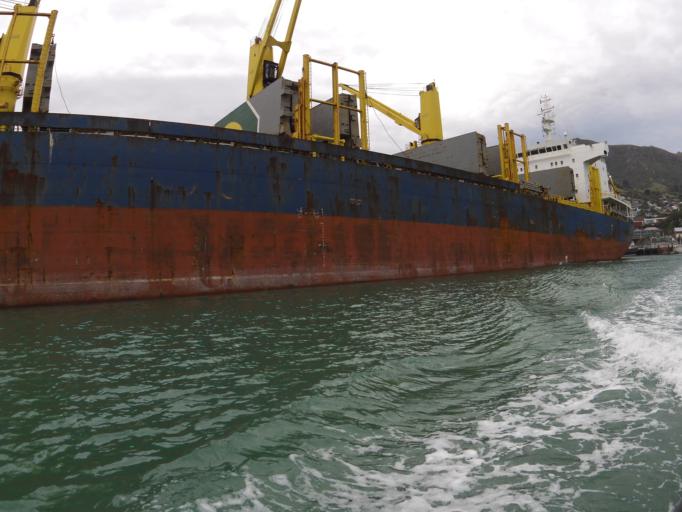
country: NZ
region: Canterbury
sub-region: Christchurch City
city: Christchurch
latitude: -43.6064
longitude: 172.7206
